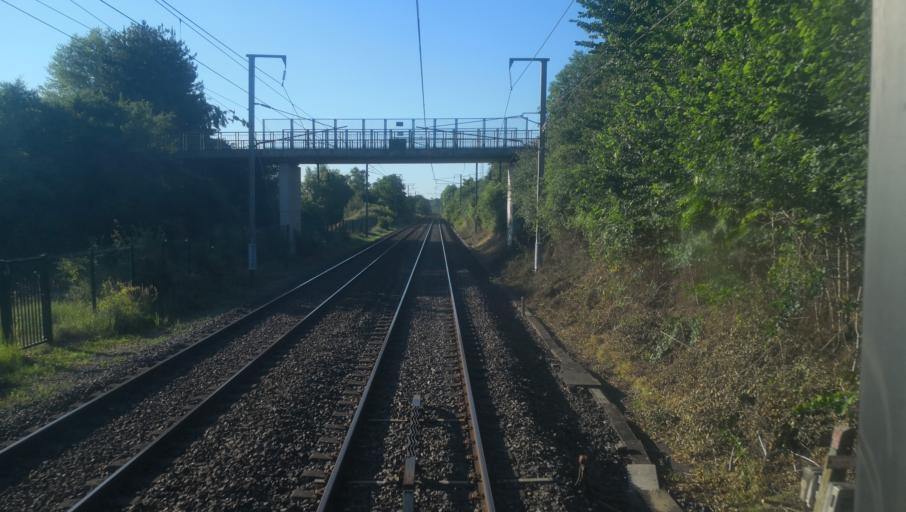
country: FR
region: Auvergne
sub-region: Departement de l'Allier
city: Trevol
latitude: 46.6183
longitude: 3.2876
